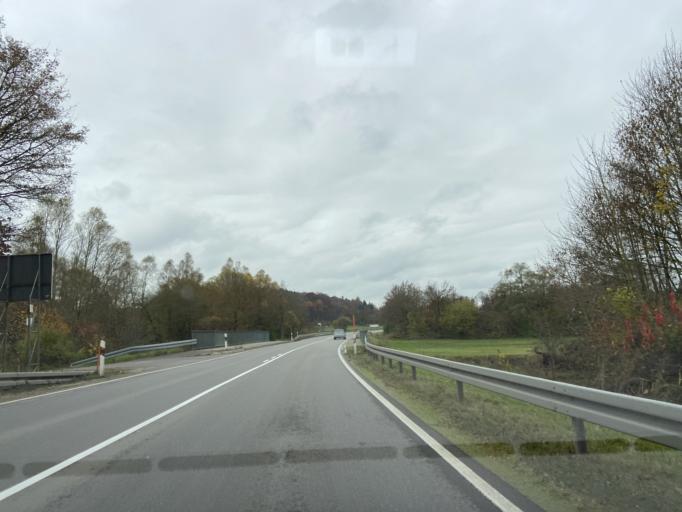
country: DE
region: Baden-Wuerttemberg
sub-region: Tuebingen Region
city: Krauchenwies
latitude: 48.0303
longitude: 9.2489
